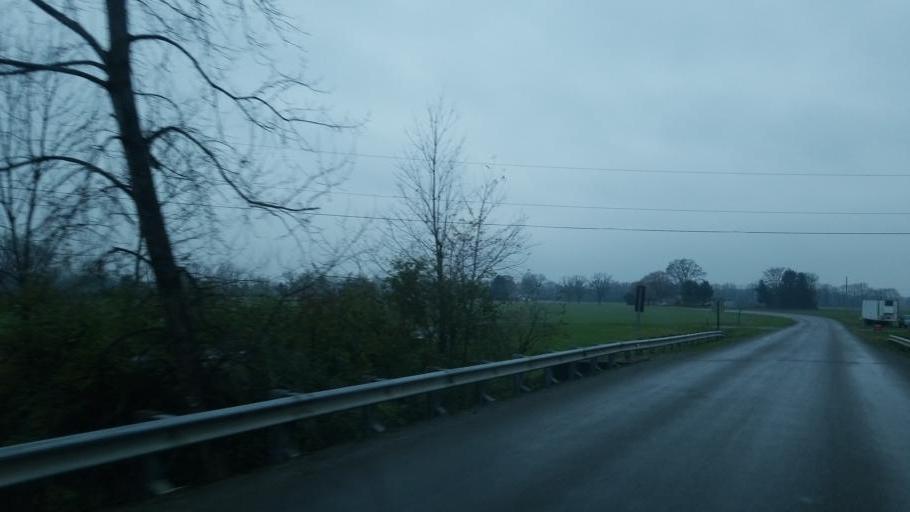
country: US
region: Ohio
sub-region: Knox County
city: Mount Vernon
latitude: 40.4060
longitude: -82.4997
